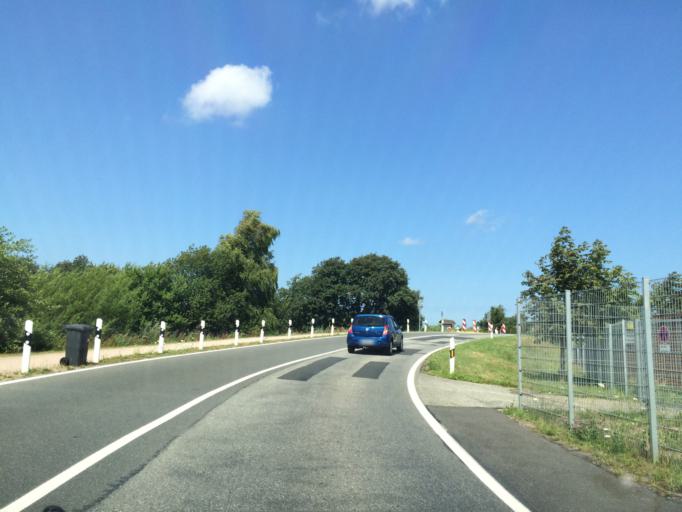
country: DE
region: Mecklenburg-Vorpommern
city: Zingst
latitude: 54.4085
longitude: 12.6655
